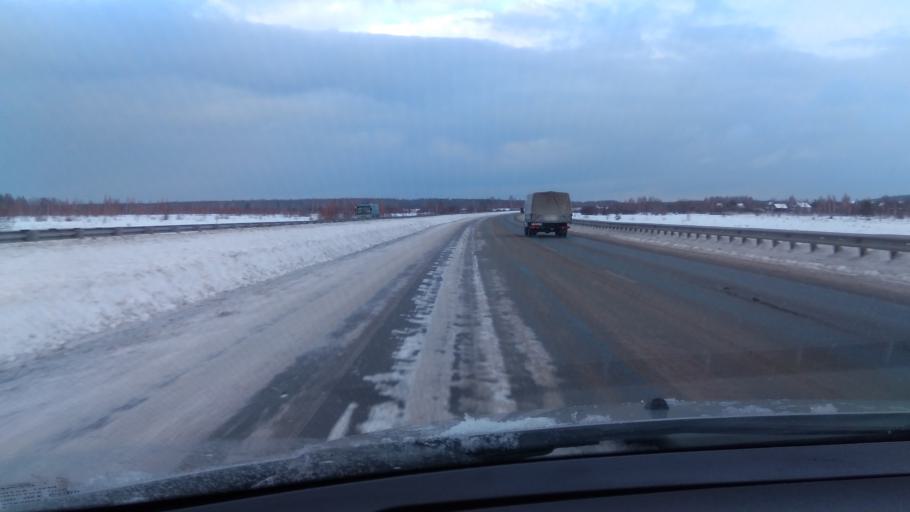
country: RU
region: Sverdlovsk
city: Nev'yansk
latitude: 57.5103
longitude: 60.1751
